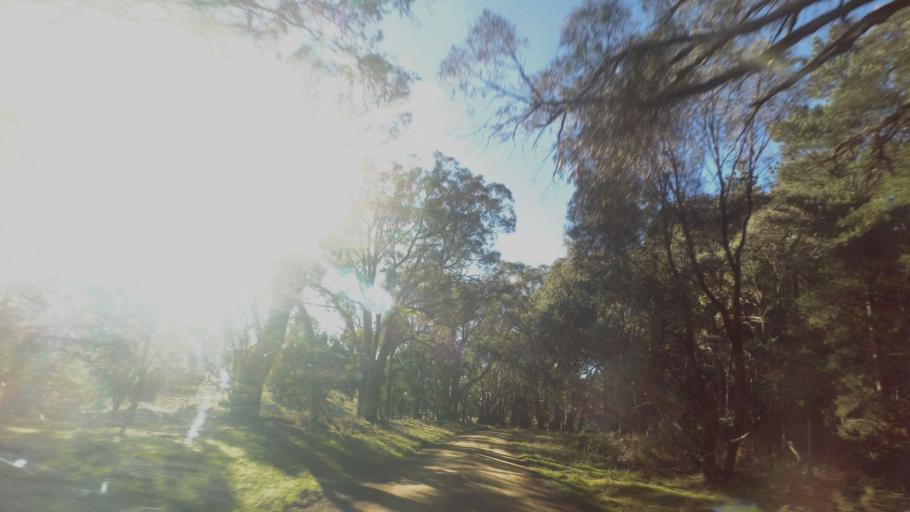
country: AU
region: Victoria
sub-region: Mount Alexander
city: Castlemaine
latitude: -37.2775
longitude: 144.3368
